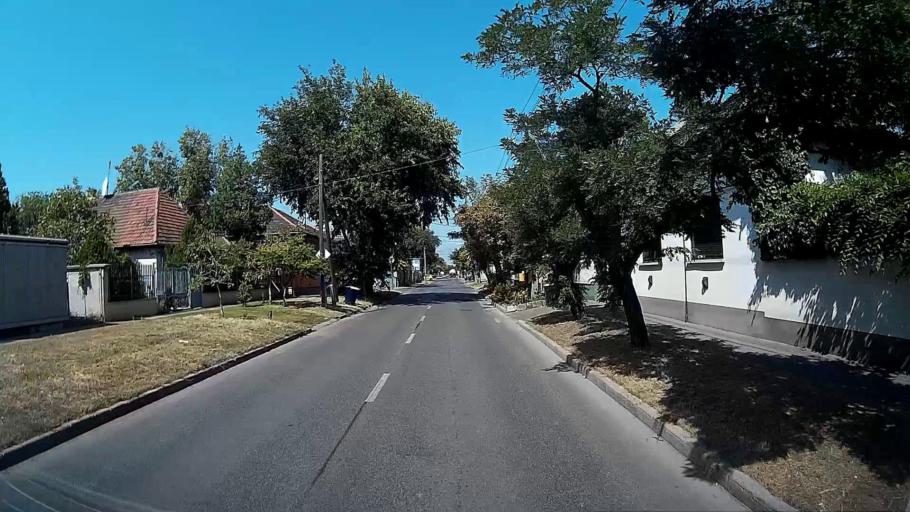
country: HU
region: Budapest
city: Budapest XX. keruelet
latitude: 47.4228
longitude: 19.1129
